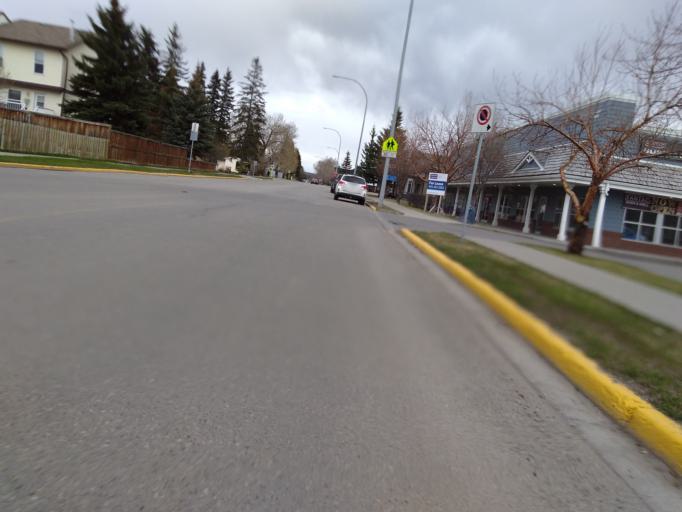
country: CA
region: Alberta
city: Cochrane
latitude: 51.1888
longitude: -114.4662
